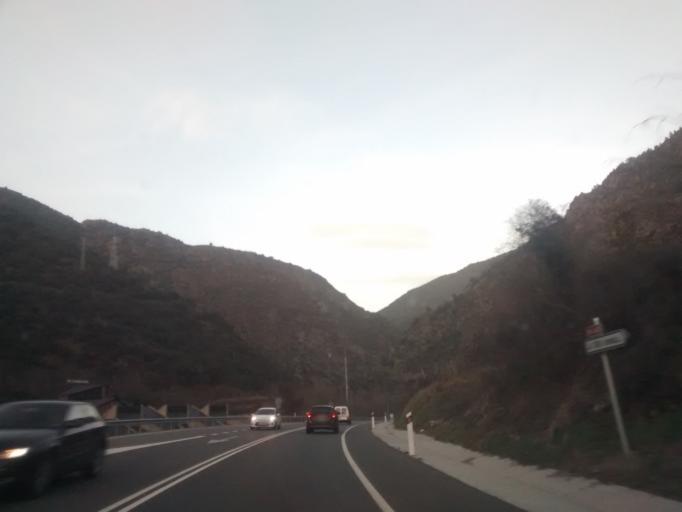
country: ES
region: Catalonia
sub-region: Provincia de Lleida
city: la Seu d'Urgell
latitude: 42.3951
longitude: 1.4612
